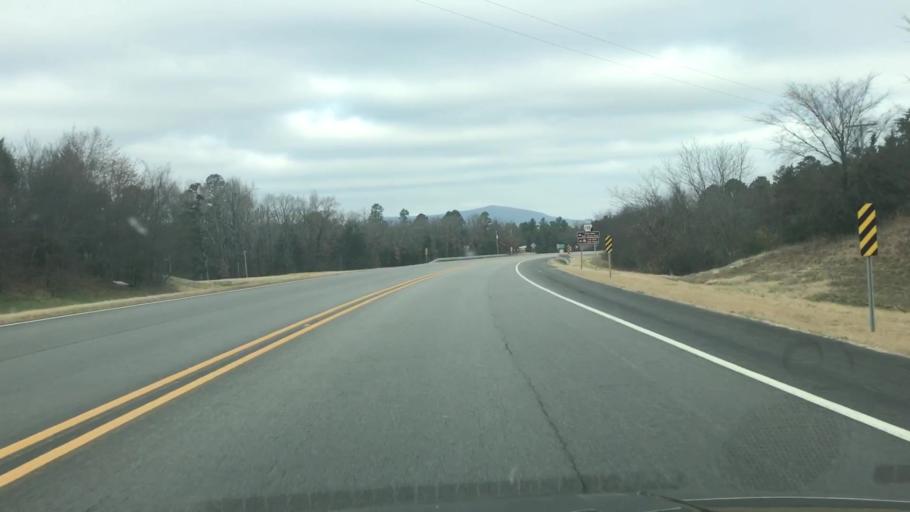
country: US
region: Arkansas
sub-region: Scott County
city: Waldron
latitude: 34.8849
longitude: -94.1067
